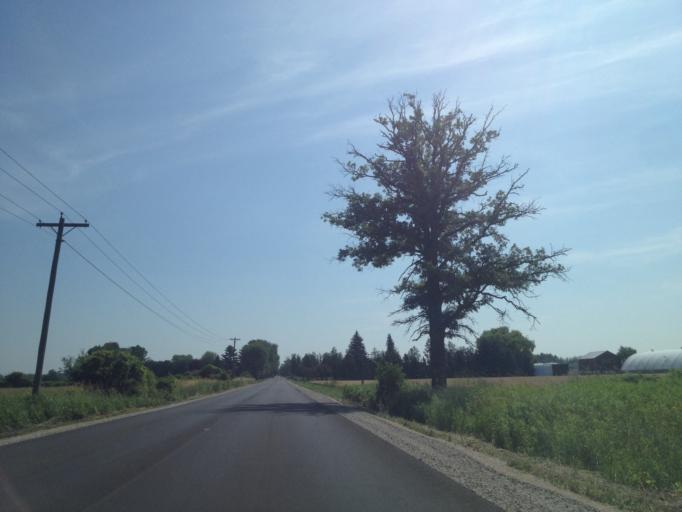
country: CA
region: Ontario
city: London
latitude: 43.0576
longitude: -81.2235
